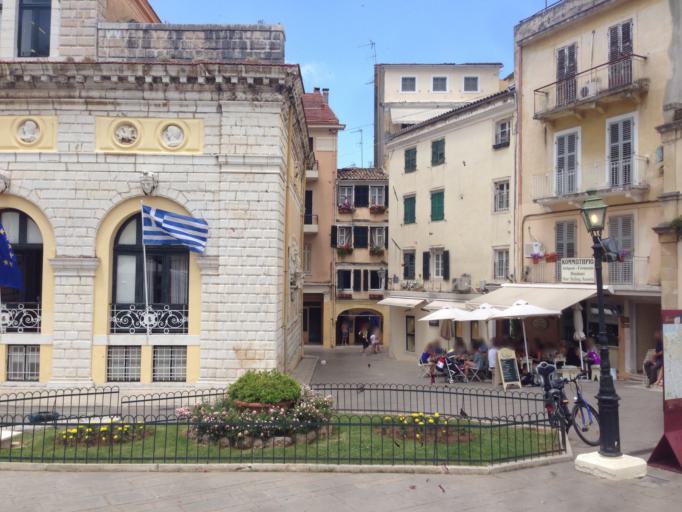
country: GR
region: Ionian Islands
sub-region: Nomos Kerkyras
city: Kerkyra
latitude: 39.6235
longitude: 19.9223
